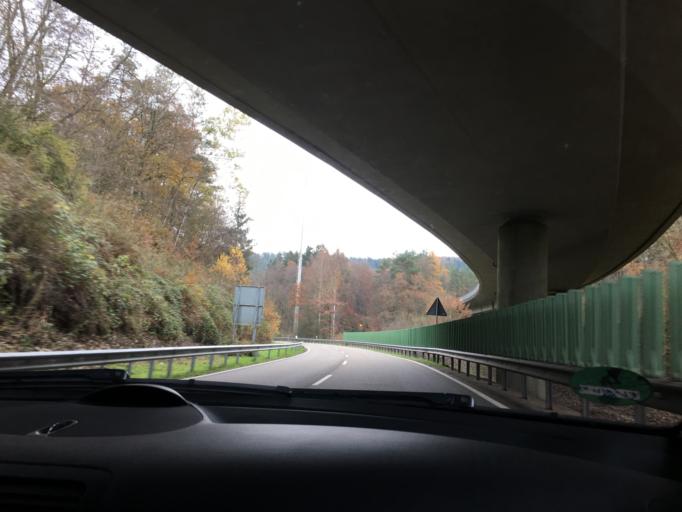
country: DE
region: Rheinland-Pfalz
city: Waldfischbach-Burgalben
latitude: 49.3003
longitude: 7.6608
